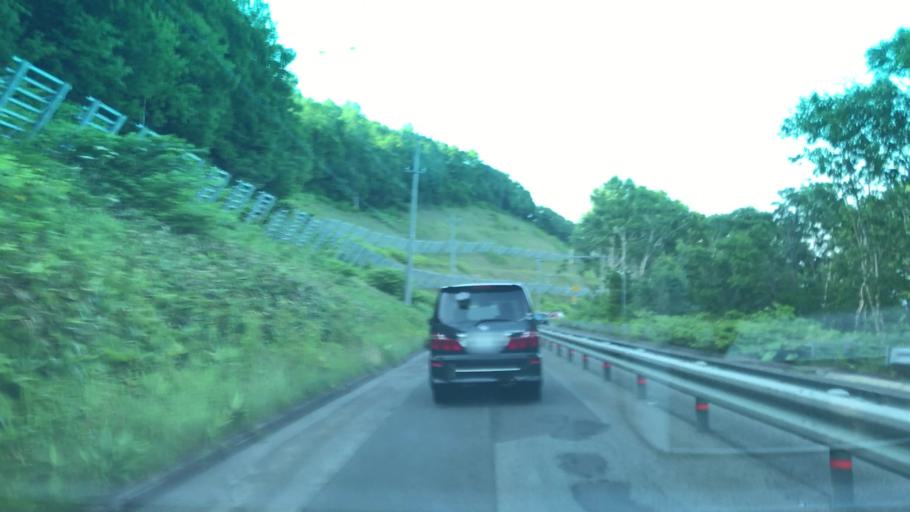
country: JP
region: Hokkaido
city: Otaru
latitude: 43.1373
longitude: 141.0137
